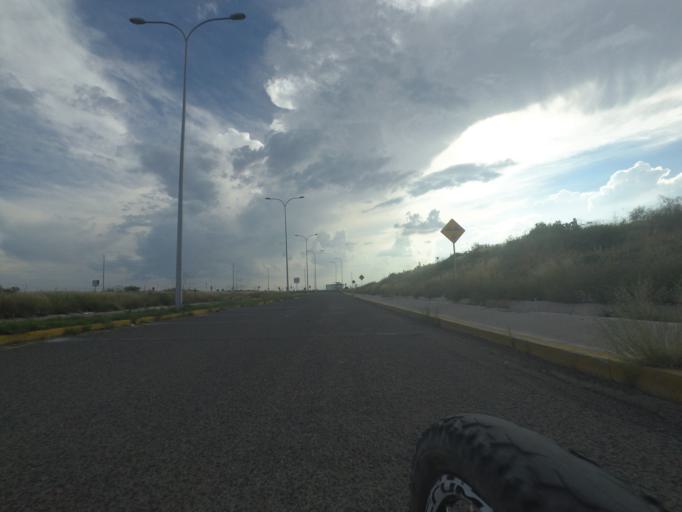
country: MX
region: Aguascalientes
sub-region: Aguascalientes
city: Penuelas (El Cienegal)
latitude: 21.7276
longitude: -102.2871
